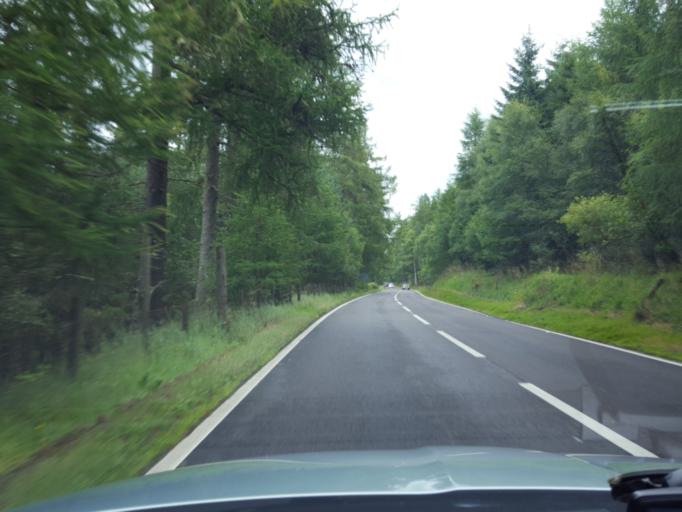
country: GB
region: Scotland
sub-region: Highland
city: Grantown on Spey
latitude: 57.3624
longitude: -3.5156
